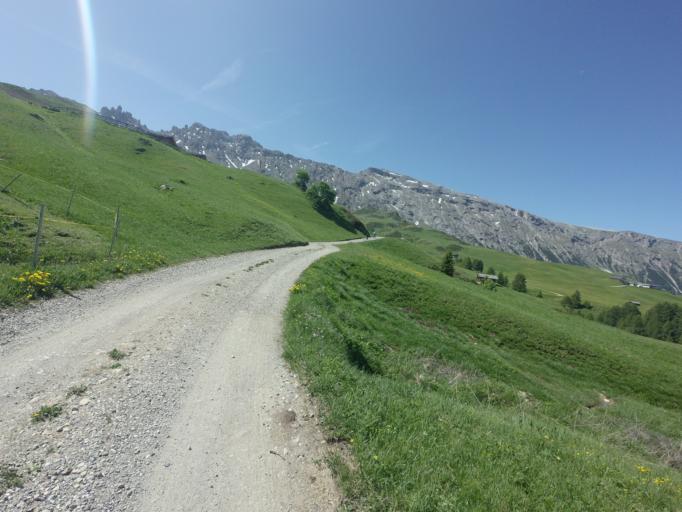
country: IT
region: Trentino-Alto Adige
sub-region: Bolzano
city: Ortisei
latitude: 46.5162
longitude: 11.6294
